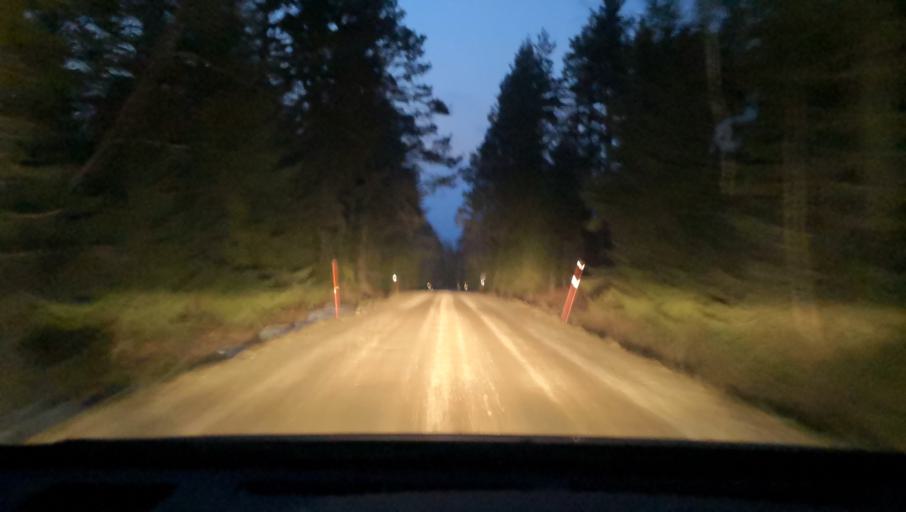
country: SE
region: OErebro
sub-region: Lindesbergs Kommun
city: Frovi
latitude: 59.6210
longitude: 15.4810
